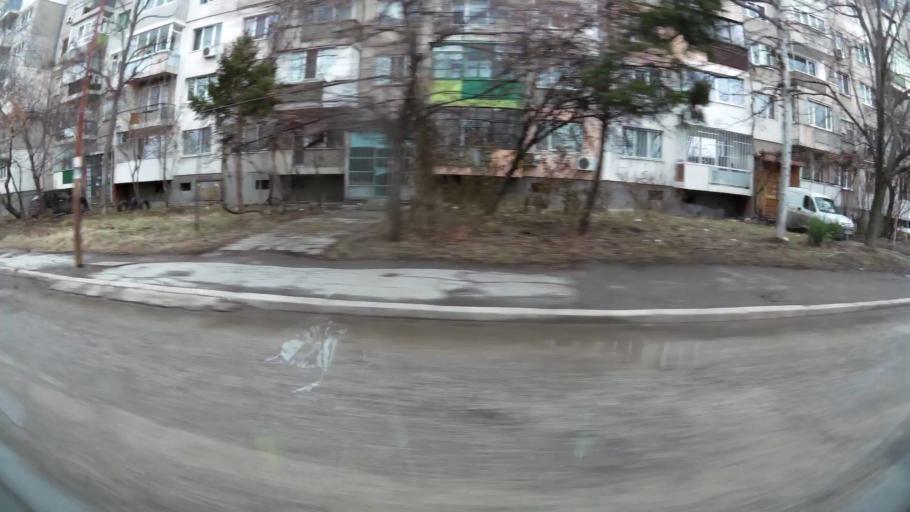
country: BG
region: Sofia-Capital
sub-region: Stolichna Obshtina
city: Sofia
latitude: 42.7286
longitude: 23.2888
